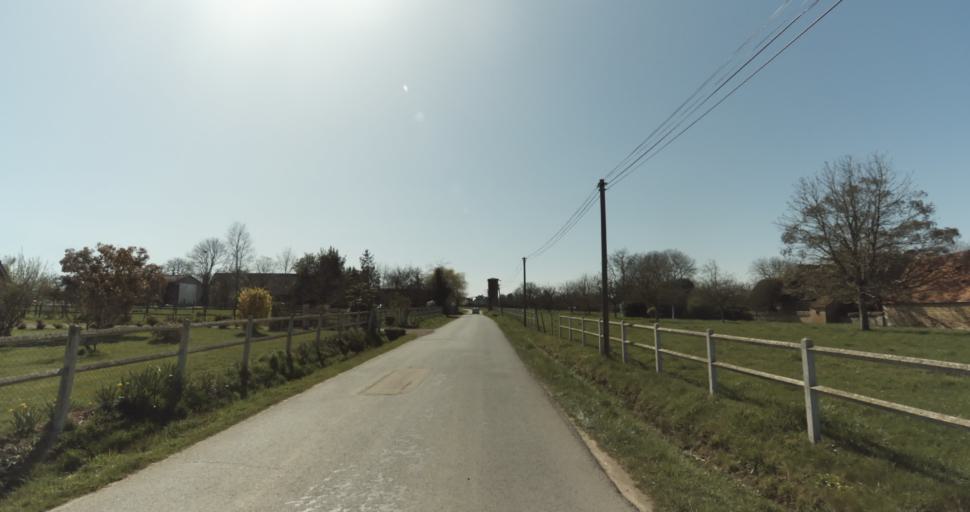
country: FR
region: Lower Normandy
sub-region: Departement du Calvados
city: Saint-Pierre-sur-Dives
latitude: 49.0162
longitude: -0.0053
